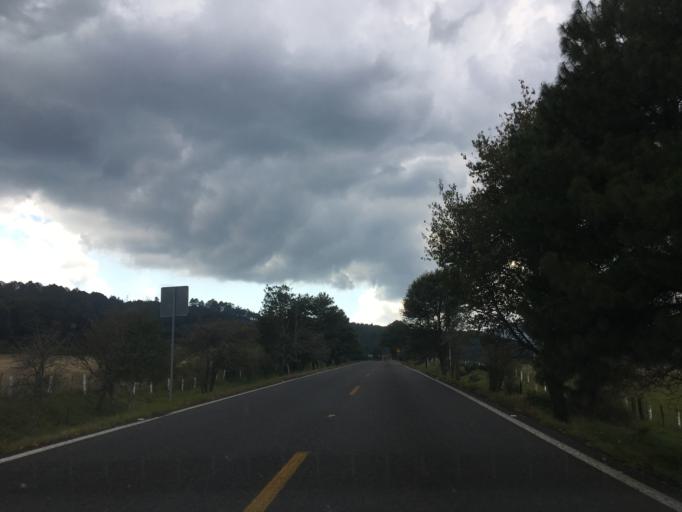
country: MX
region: Michoacan
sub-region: Patzcuaro
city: Santa Maria Huiramangaro (San Juan Tumbio)
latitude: 19.4873
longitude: -101.7274
